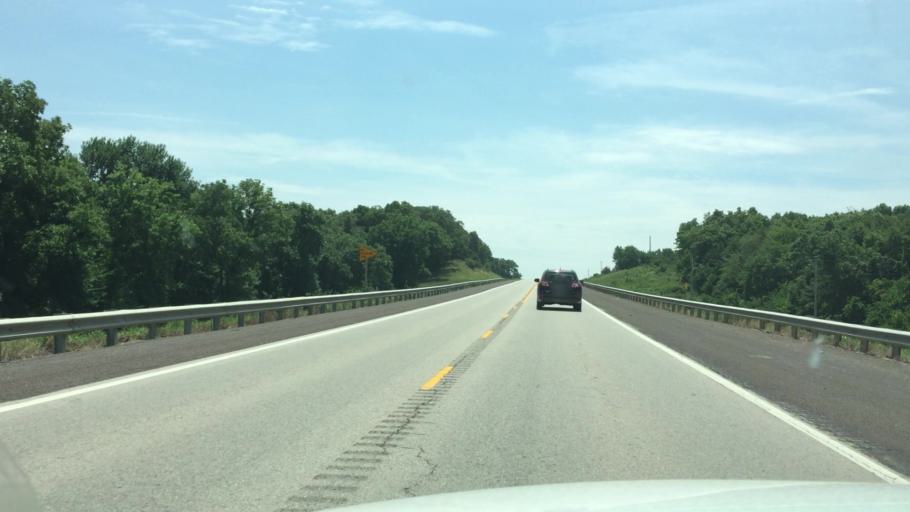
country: US
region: Kansas
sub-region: Jackson County
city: Holton
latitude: 39.5452
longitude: -95.7483
